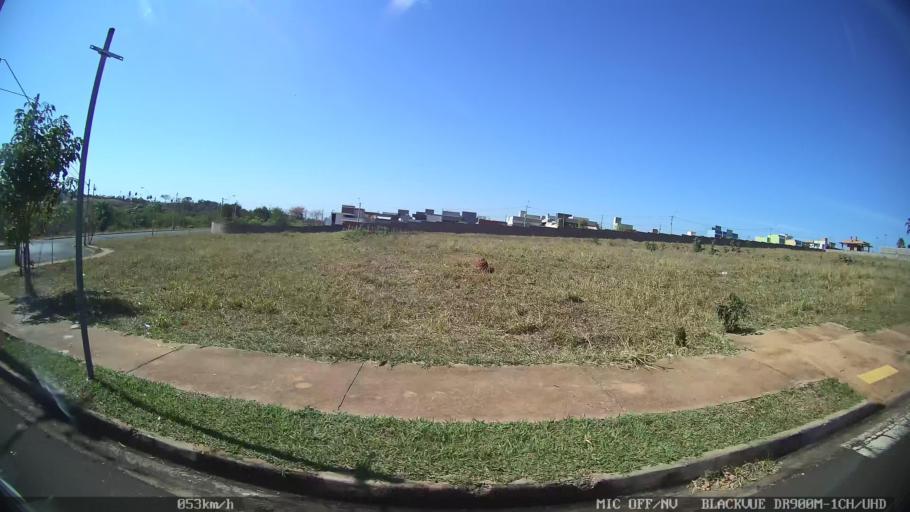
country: BR
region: Sao Paulo
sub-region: Sao Jose Do Rio Preto
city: Sao Jose do Rio Preto
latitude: -20.7624
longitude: -49.4200
